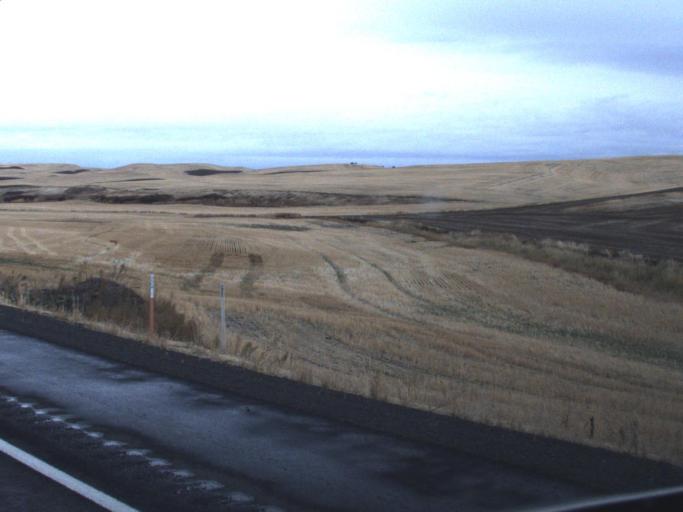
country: US
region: Washington
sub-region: Asotin County
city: Clarkston
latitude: 46.5561
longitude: -117.1038
